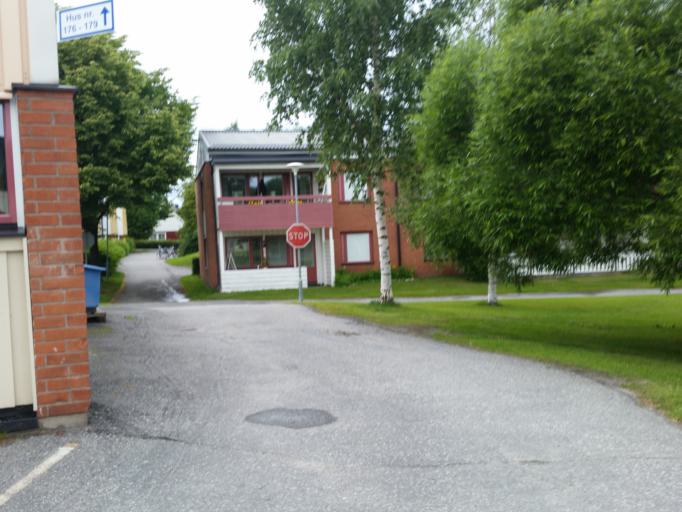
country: SE
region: Vaesterbotten
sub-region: Umea Kommun
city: Ersmark
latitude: 63.8458
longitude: 20.3024
